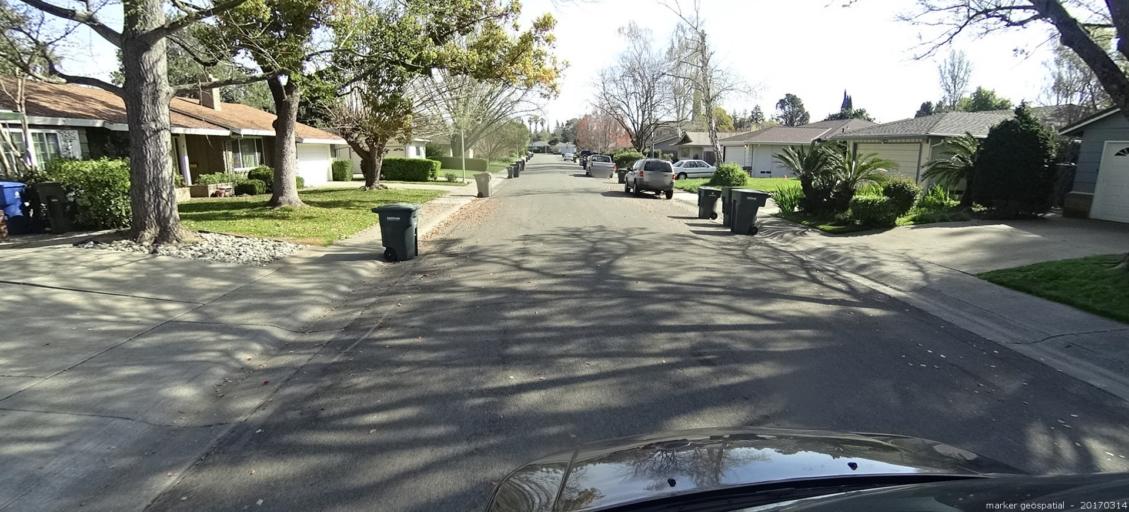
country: US
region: California
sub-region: Yolo County
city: West Sacramento
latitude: 38.5121
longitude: -121.5276
